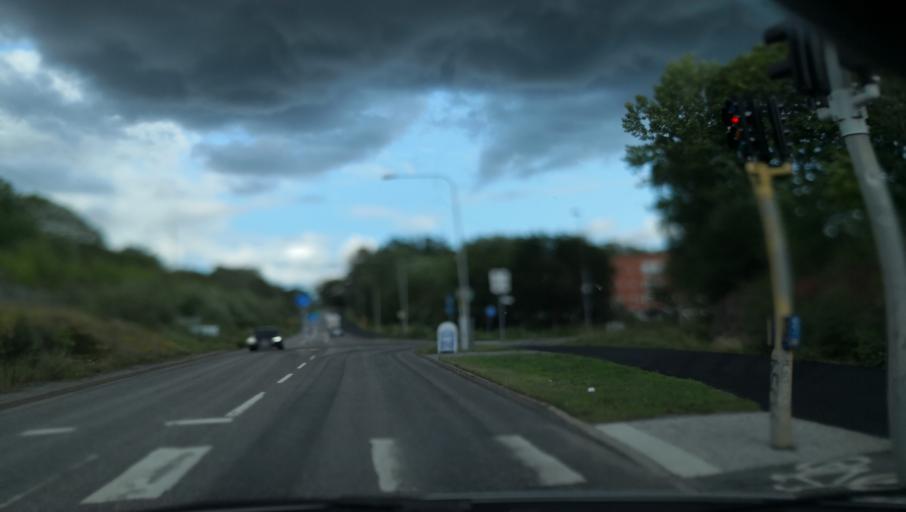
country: SE
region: Stockholm
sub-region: Stockholms Kommun
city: Arsta
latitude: 59.2407
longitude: 18.0852
